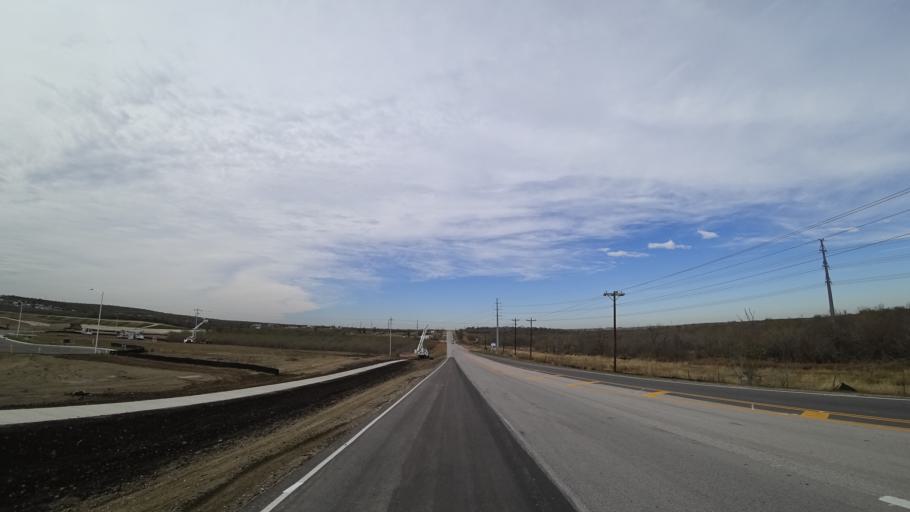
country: US
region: Texas
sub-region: Travis County
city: Garfield
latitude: 30.1527
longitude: -97.5884
